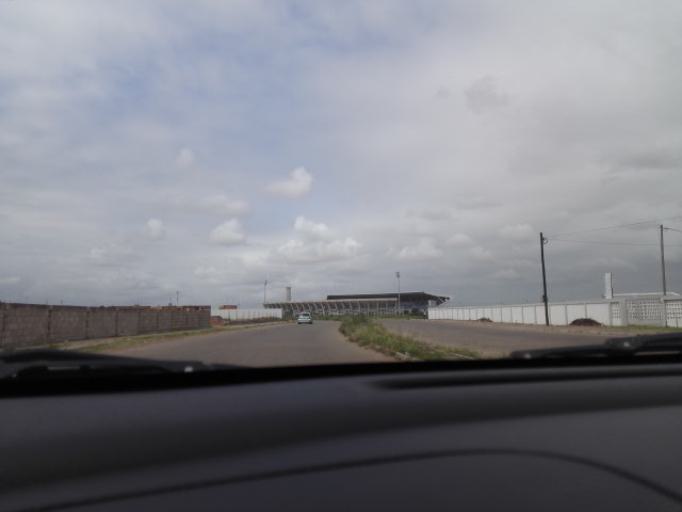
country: MZ
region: Maputo City
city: Maputo
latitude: -25.8235
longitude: 32.5820
